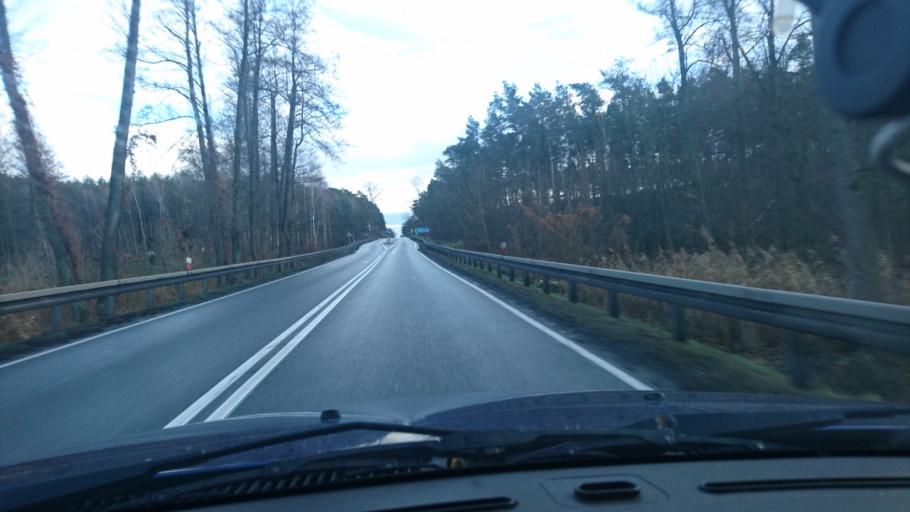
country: PL
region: Greater Poland Voivodeship
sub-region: Powiat kepinski
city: Kepno
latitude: 51.3274
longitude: 17.9622
